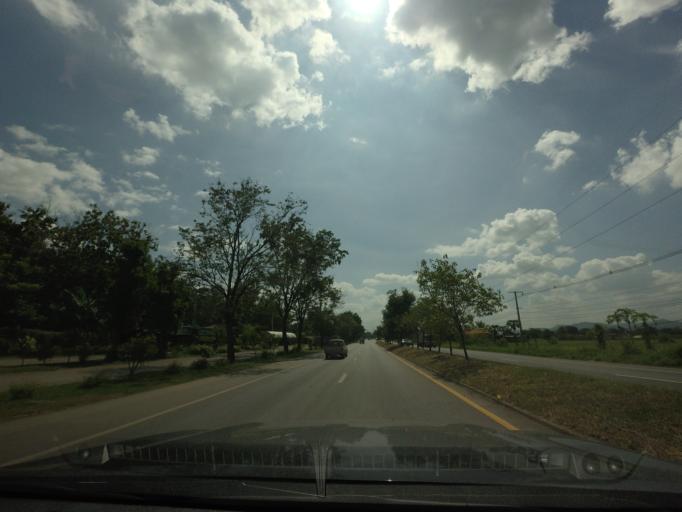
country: TH
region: Phetchabun
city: Nong Phai
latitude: 15.9449
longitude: 101.0328
